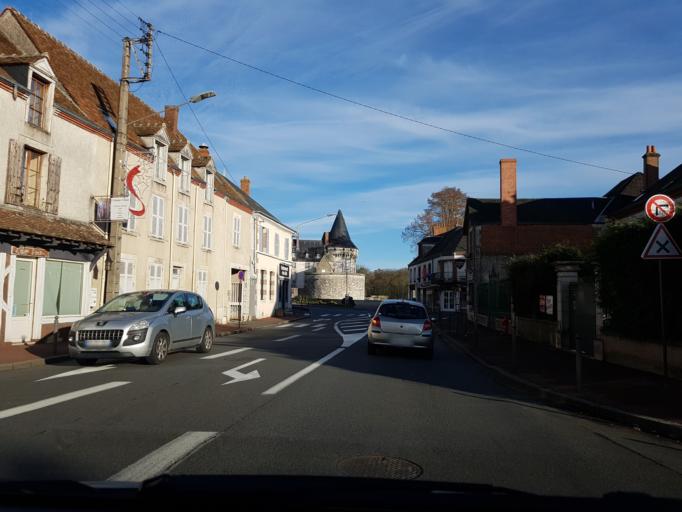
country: FR
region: Centre
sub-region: Departement du Loiret
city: Sully-sur-Loire
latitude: 47.7670
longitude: 2.3734
